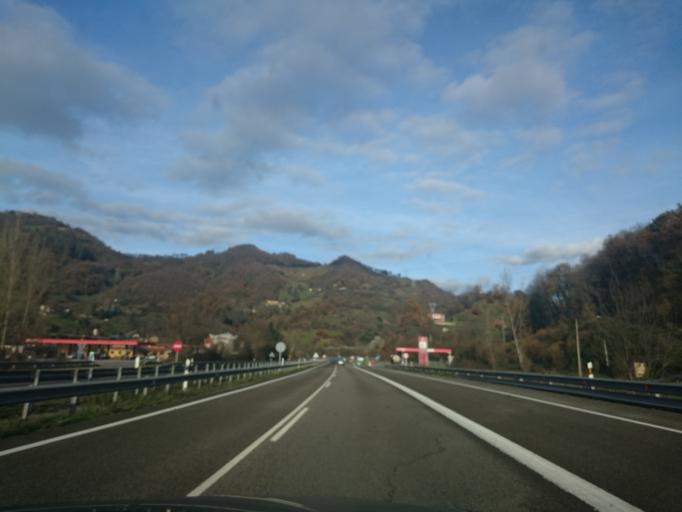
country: ES
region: Asturias
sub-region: Province of Asturias
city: Pola de Lena
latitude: 43.1802
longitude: -5.8115
